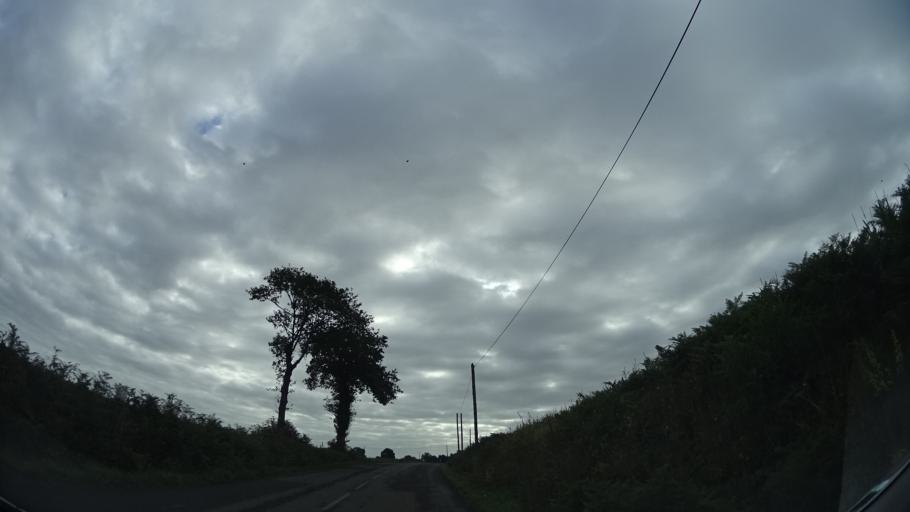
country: FR
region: Brittany
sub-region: Departement d'Ille-et-Vilaine
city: Montreuil-sur-Ille
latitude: 48.3388
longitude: -1.6574
